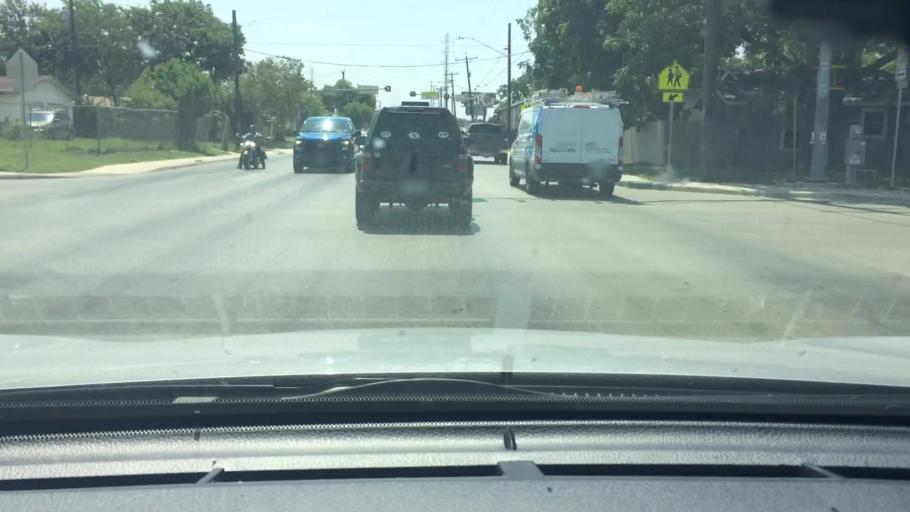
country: US
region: Texas
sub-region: Bexar County
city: San Antonio
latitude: 29.3634
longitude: -98.4392
